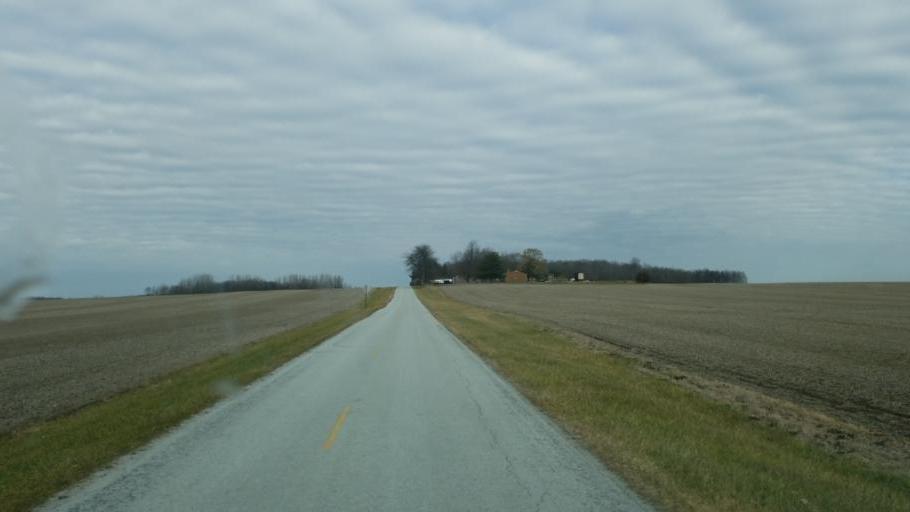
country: US
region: Ohio
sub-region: Hardin County
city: Kenton
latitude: 40.6100
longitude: -83.4202
